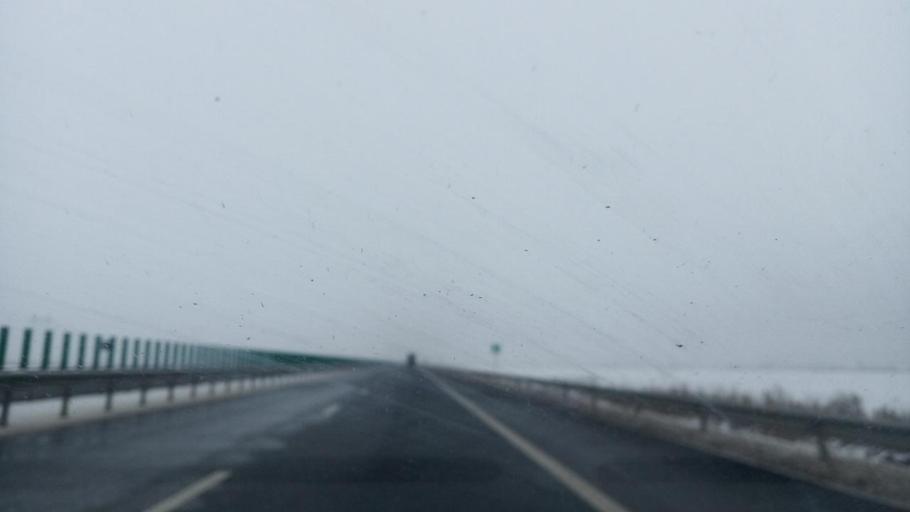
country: RO
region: Bacau
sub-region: Comuna Letea Veche
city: Holt
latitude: 46.5640
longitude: 26.9668
